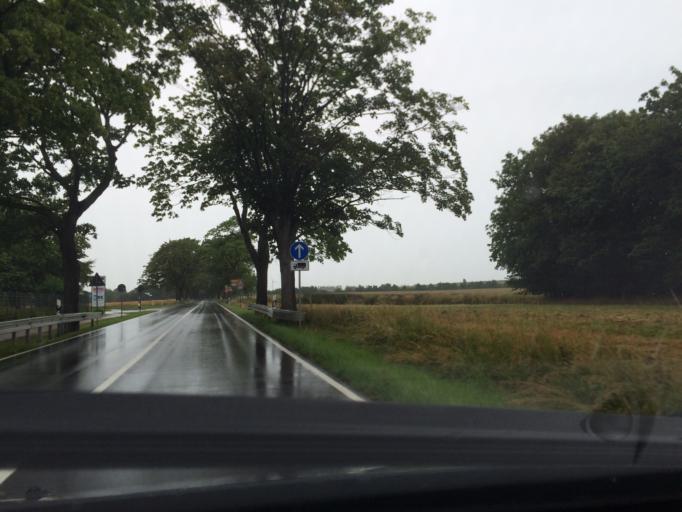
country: DE
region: Mecklenburg-Vorpommern
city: Kramerhof
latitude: 54.3399
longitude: 13.0544
